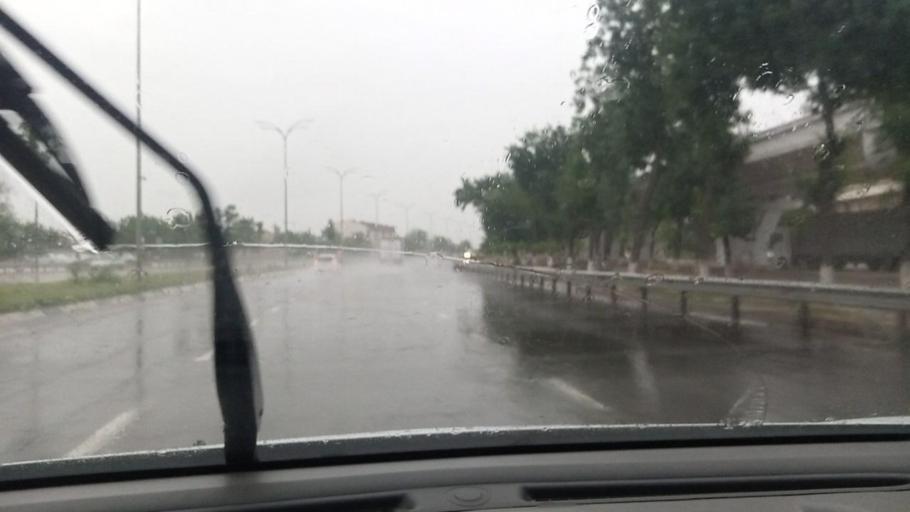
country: UZ
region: Toshkent Shahri
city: Bektemir
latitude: 41.2893
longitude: 69.3591
